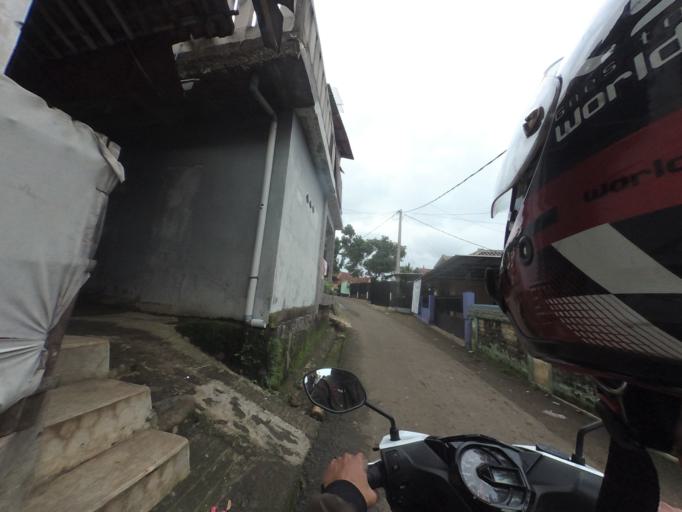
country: ID
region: West Java
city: Bogor
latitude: -6.6152
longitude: 106.7369
